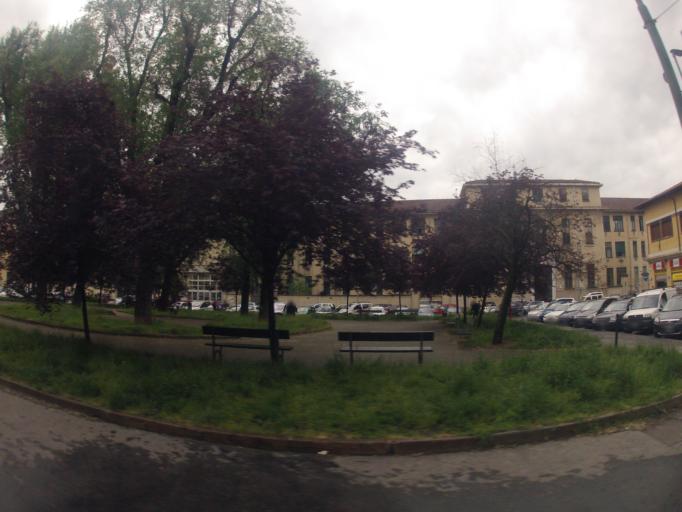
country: IT
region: Piedmont
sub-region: Provincia di Torino
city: Turin
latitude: 45.0389
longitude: 7.6721
